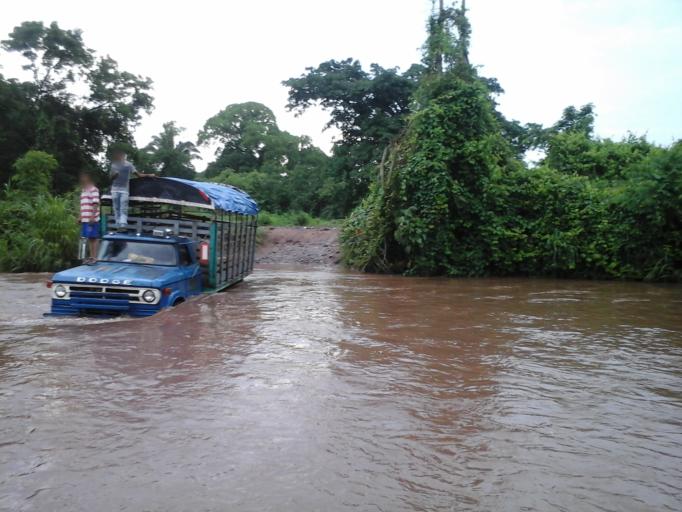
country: CO
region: Cesar
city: Agustin Codazzi
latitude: 9.9034
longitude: -73.2239
